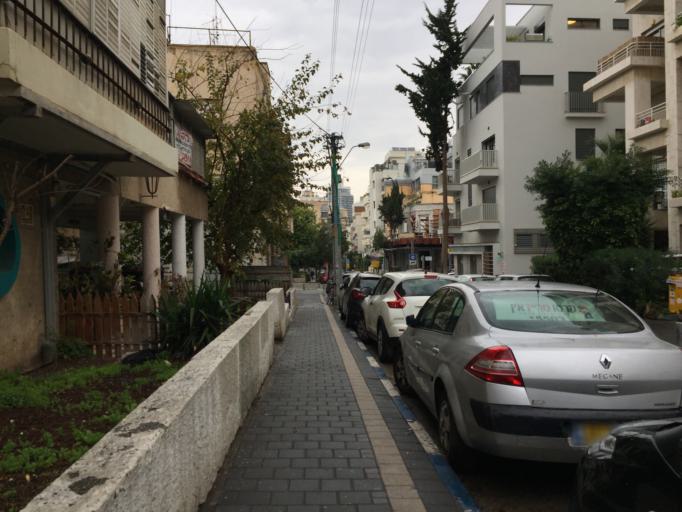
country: IL
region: Tel Aviv
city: Tel Aviv
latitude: 32.0687
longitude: 34.7731
